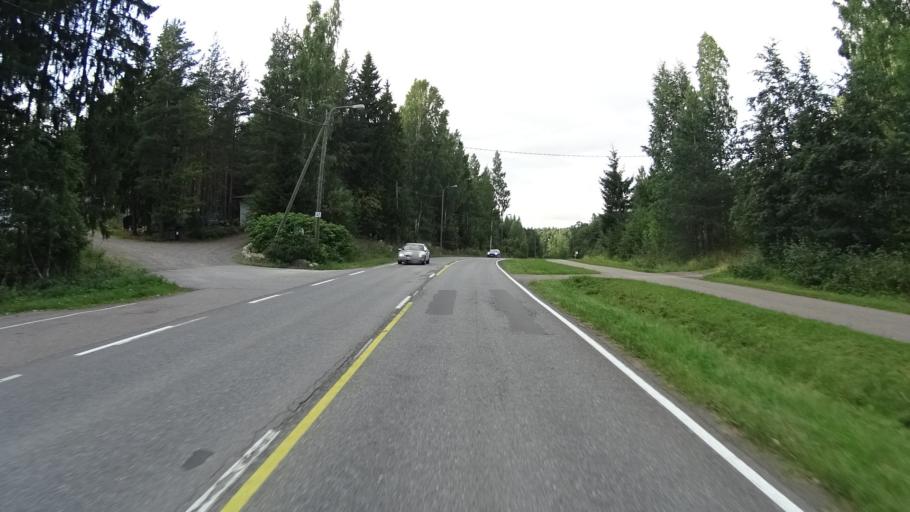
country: FI
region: Uusimaa
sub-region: Helsinki
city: Nurmijaervi
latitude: 60.3393
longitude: 24.8646
